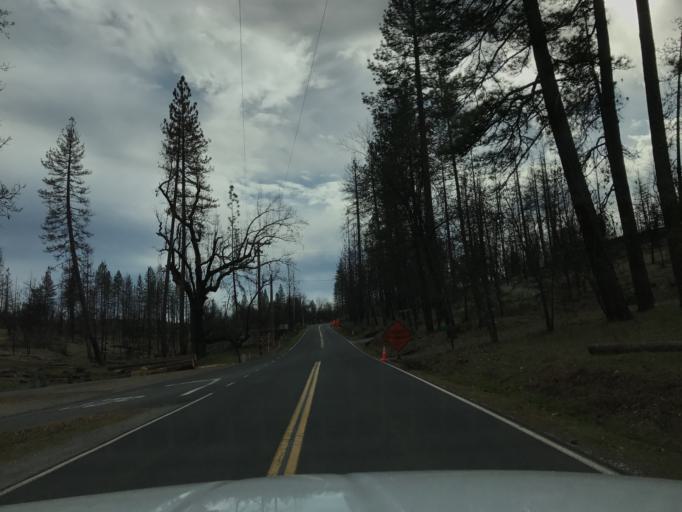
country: US
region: California
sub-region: Calaveras County
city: Mountain Ranch
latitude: 38.2430
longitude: -120.5164
